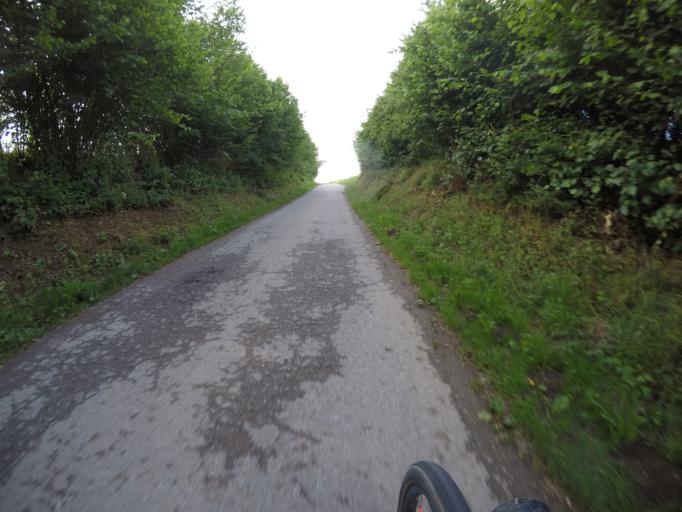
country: DE
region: Baden-Wuerttemberg
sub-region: Regierungsbezirk Stuttgart
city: Schlaitdorf
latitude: 48.6078
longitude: 9.2190
